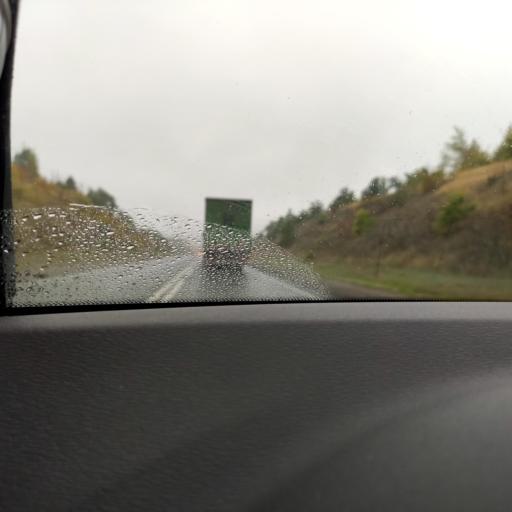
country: RU
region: Samara
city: Yelkhovka
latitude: 53.7049
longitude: 50.2270
